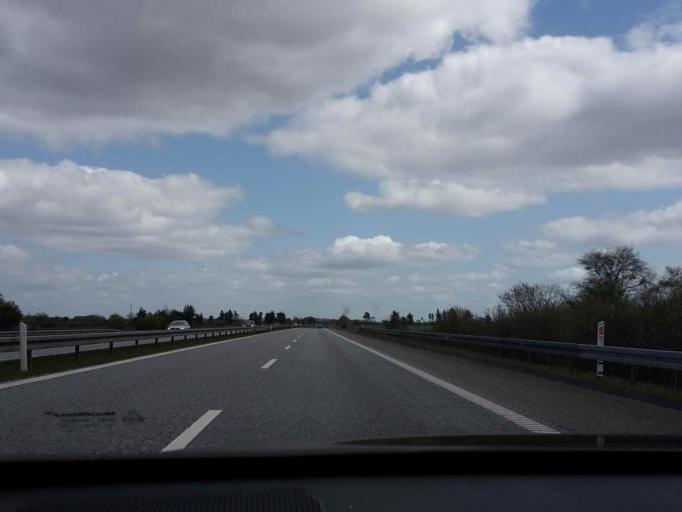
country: DK
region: South Denmark
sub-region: Esbjerg Kommune
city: Bramming
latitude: 55.5091
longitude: 8.7336
